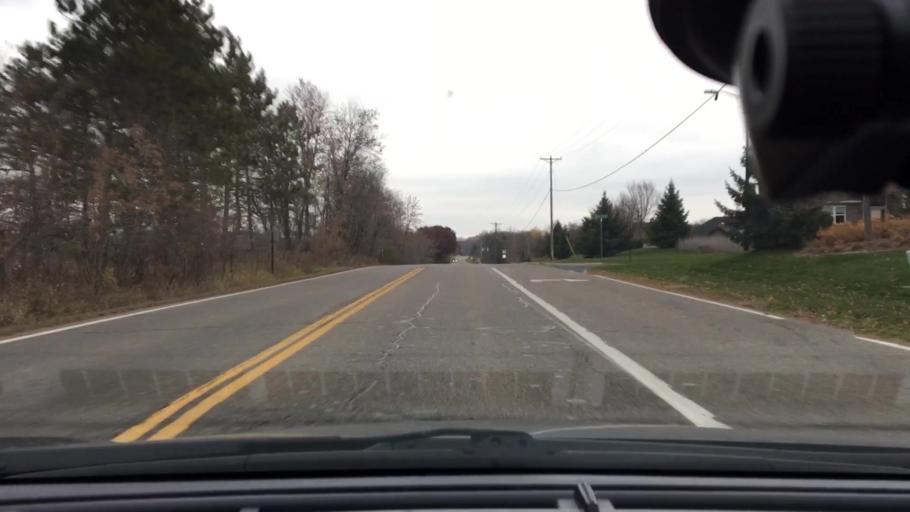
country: US
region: Minnesota
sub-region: Hennepin County
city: Corcoran
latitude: 45.0993
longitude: -93.5123
